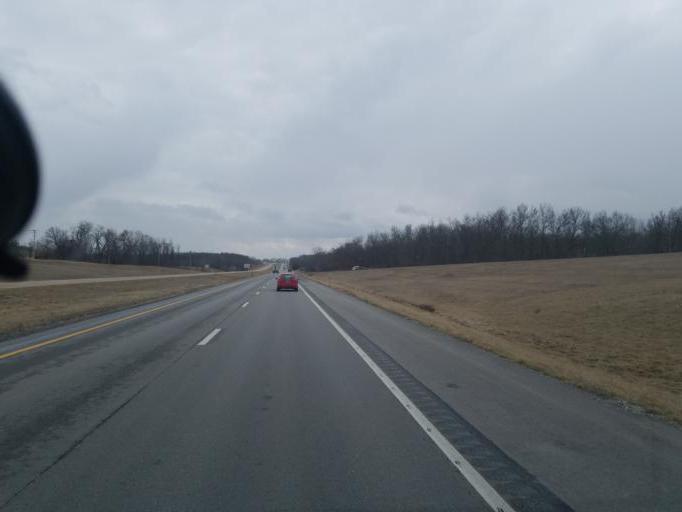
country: US
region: Missouri
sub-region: Randolph County
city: Moberly
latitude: 39.3937
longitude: -92.4132
